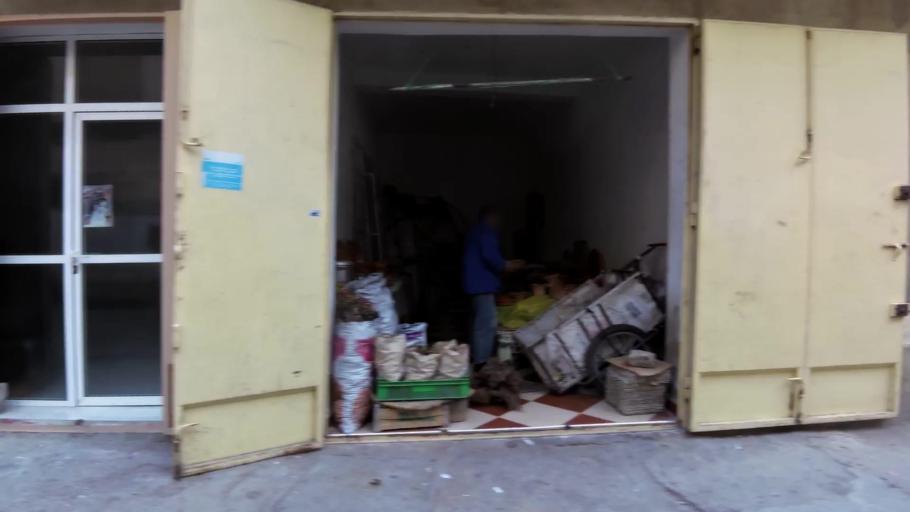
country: MA
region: Tanger-Tetouan
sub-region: Tanger-Assilah
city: Tangier
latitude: 35.7465
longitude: -5.8050
